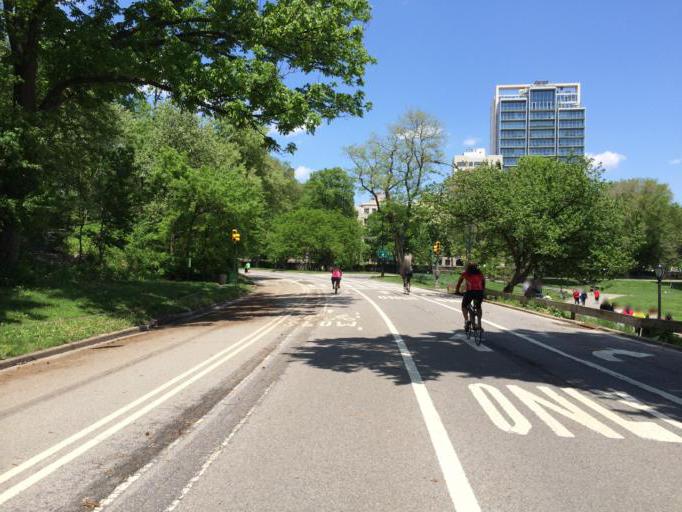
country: US
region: New York
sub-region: New York County
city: Manhattan
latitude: 40.7973
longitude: -73.9546
